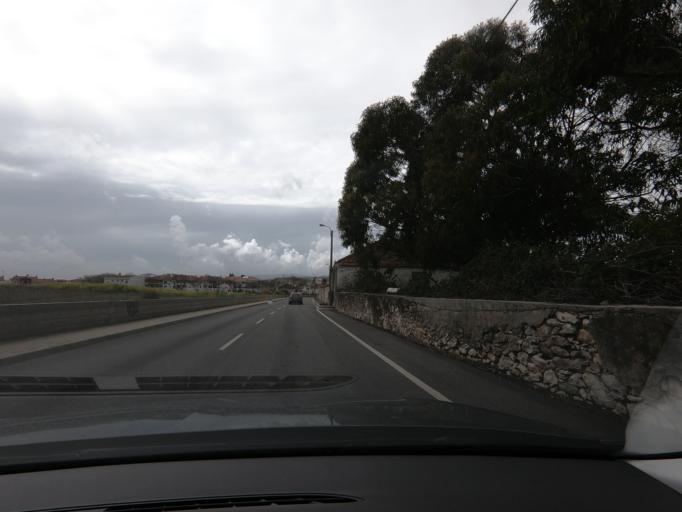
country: PT
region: Lisbon
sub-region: Cascais
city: Sao Domingos de Rana
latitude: 38.7352
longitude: -9.3339
